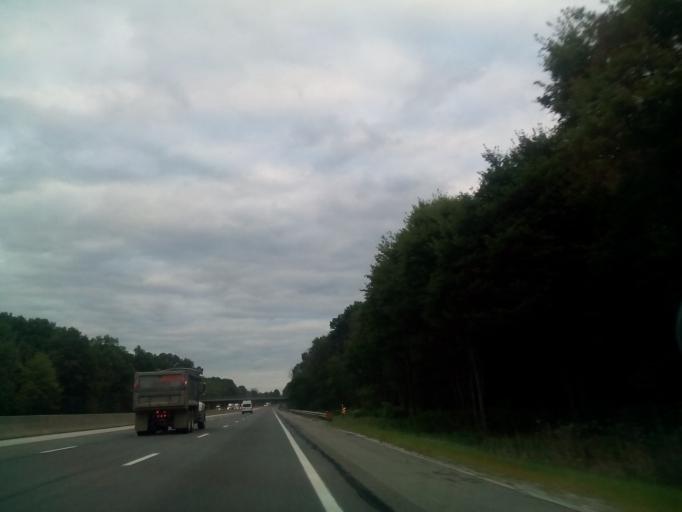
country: US
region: Ohio
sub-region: Portage County
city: Windham
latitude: 41.2412
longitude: -81.0023
